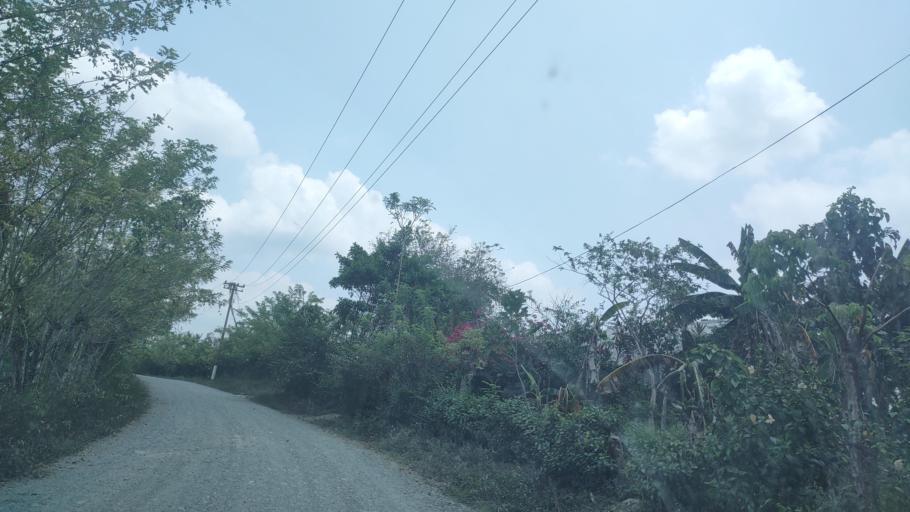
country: MX
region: Tabasco
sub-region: Huimanguillo
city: Francisco Rueda
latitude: 17.5871
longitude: -93.9586
